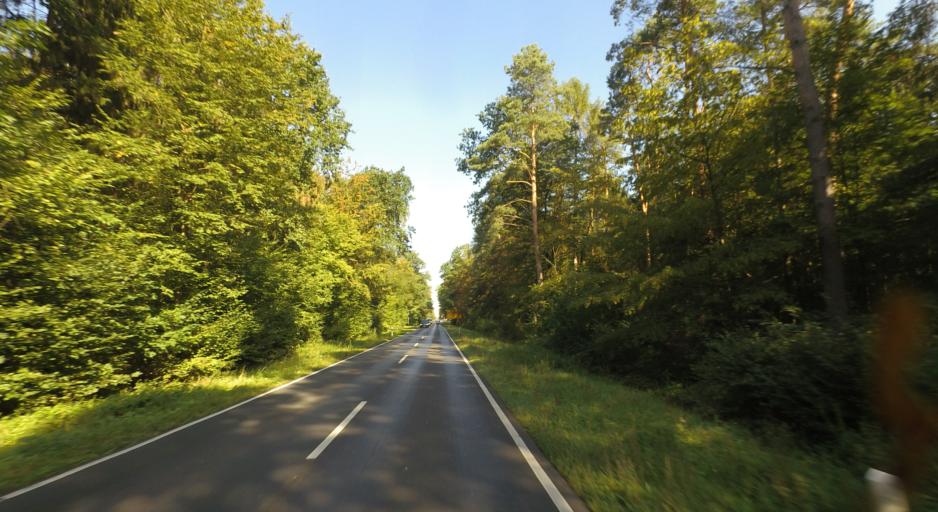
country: DE
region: Hesse
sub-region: Regierungsbezirk Darmstadt
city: Seligenstadt
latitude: 50.0264
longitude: 8.9887
